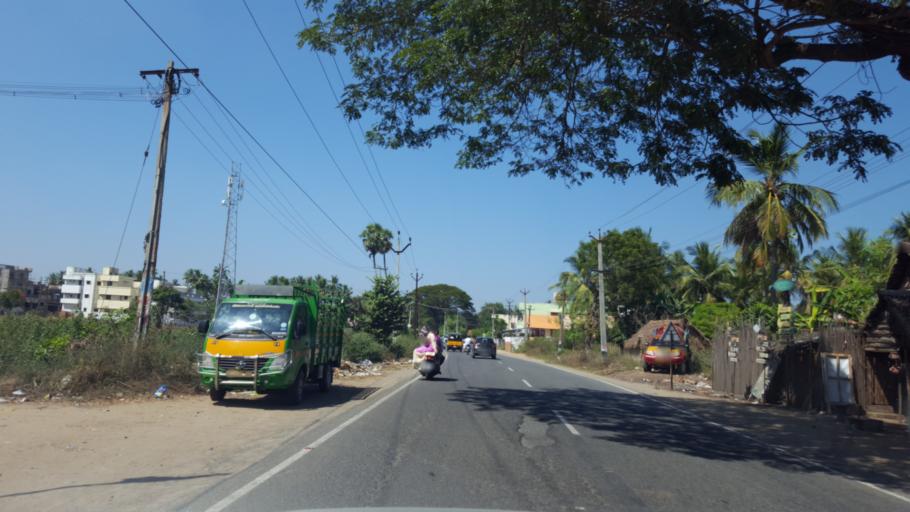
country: IN
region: Tamil Nadu
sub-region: Kancheepuram
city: Chengalpattu
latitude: 12.7091
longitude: 79.9612
